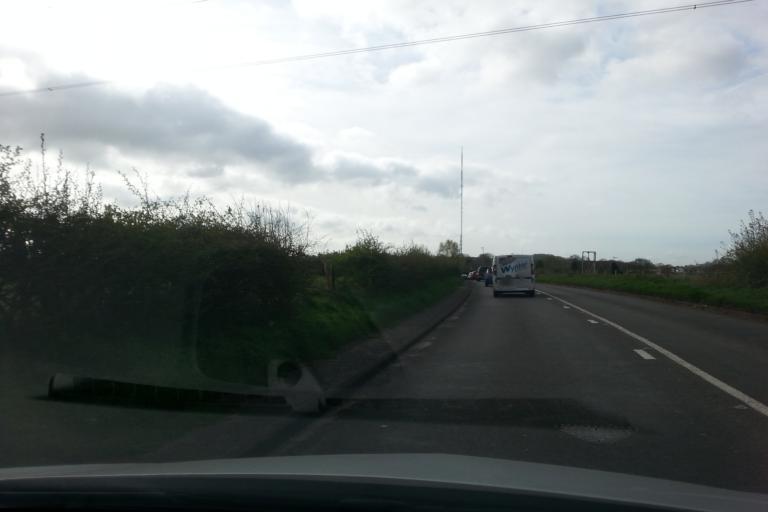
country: GB
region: England
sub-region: Staffordshire
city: Shenstone
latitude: 52.6144
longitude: -1.8387
